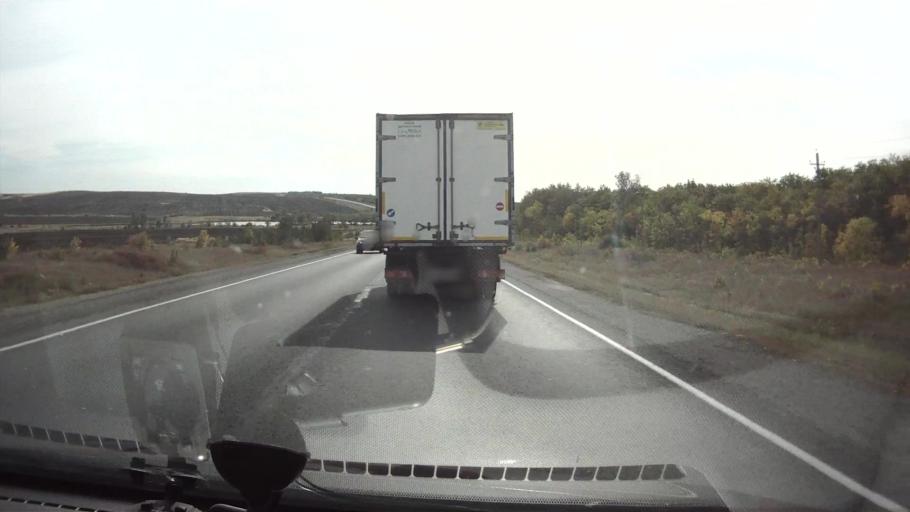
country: RU
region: Saratov
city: Alekseyevka
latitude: 52.2548
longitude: 47.9157
